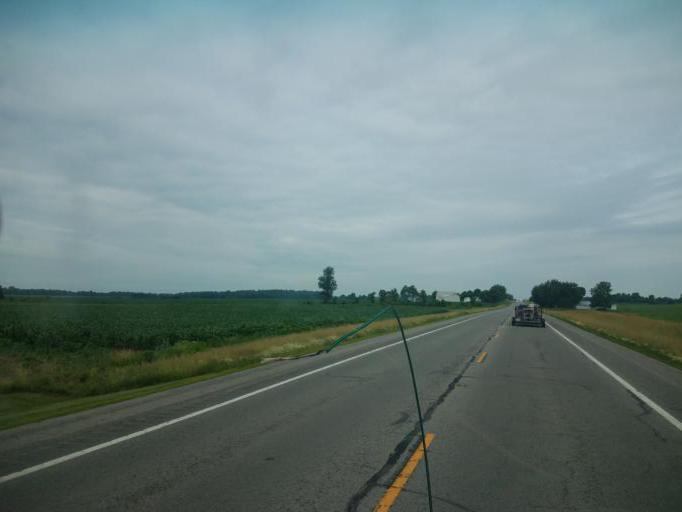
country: US
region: Ohio
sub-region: Hardin County
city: Kenton
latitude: 40.6986
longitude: -83.7164
